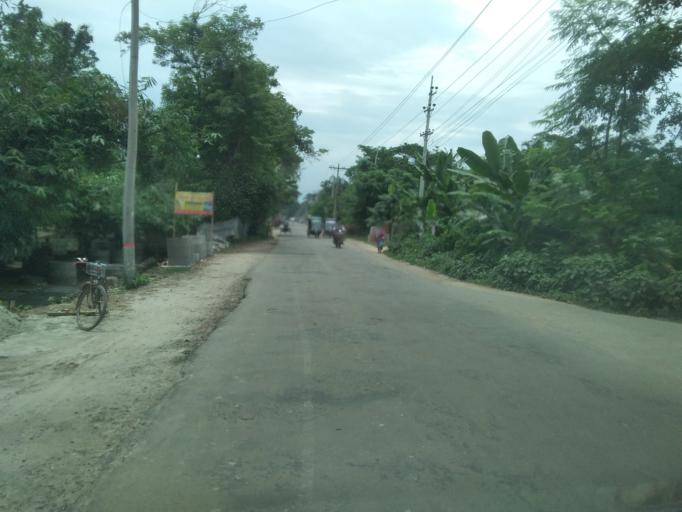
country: IN
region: West Bengal
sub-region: North 24 Parganas
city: Taki
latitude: 22.5579
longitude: 89.0057
